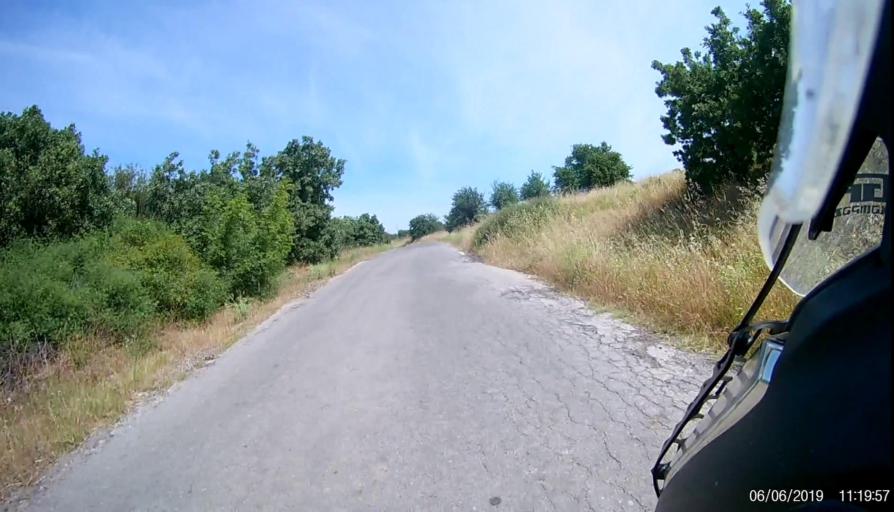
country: TR
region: Canakkale
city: Gulpinar
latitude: 39.6617
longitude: 26.1640
